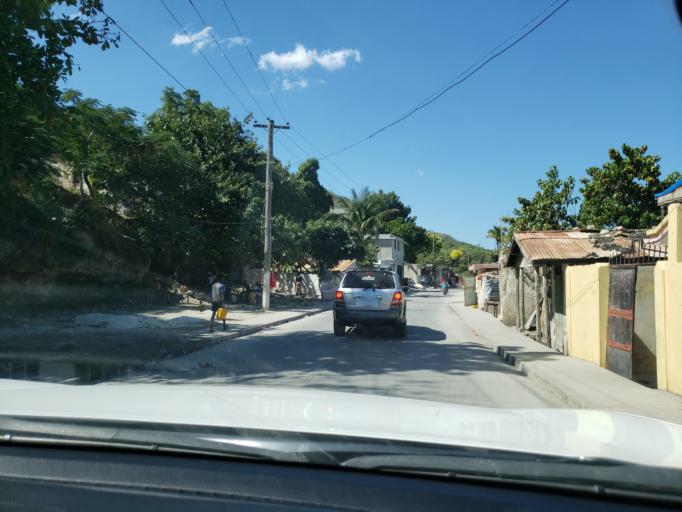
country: HT
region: Nippes
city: Miragoane
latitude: 18.4437
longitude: -73.0958
